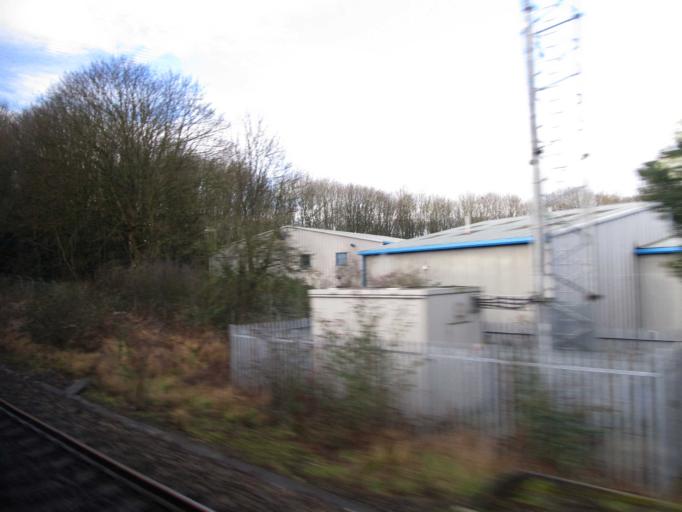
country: GB
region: England
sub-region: Hampshire
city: Basingstoke
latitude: 51.2755
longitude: -1.0694
